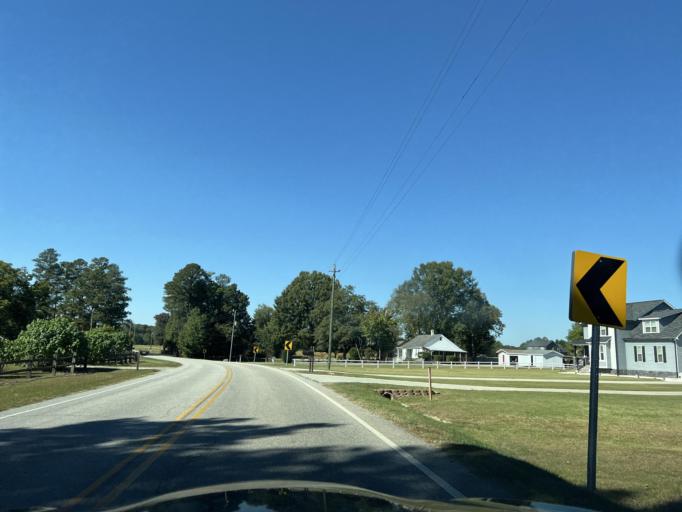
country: US
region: North Carolina
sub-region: Johnston County
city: Clayton
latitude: 35.6718
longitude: -78.4811
